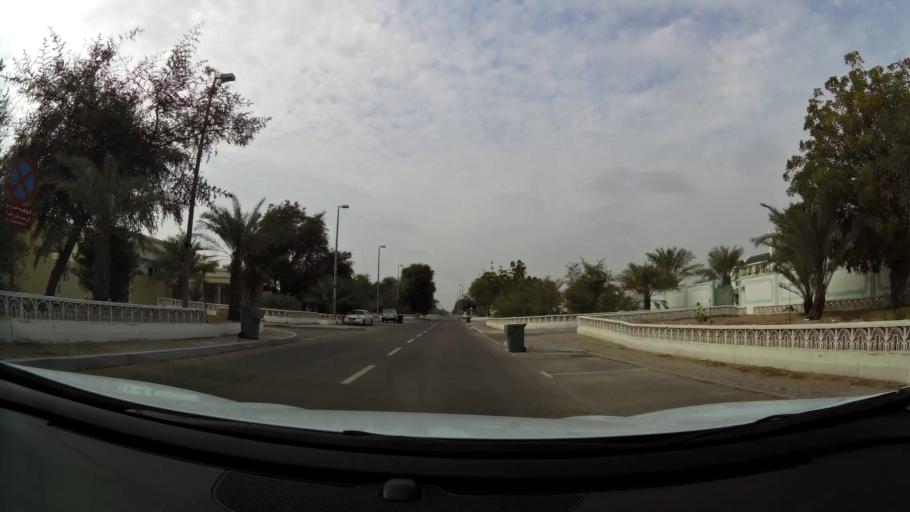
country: AE
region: Abu Dhabi
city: Abu Dhabi
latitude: 24.6445
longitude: 54.7303
